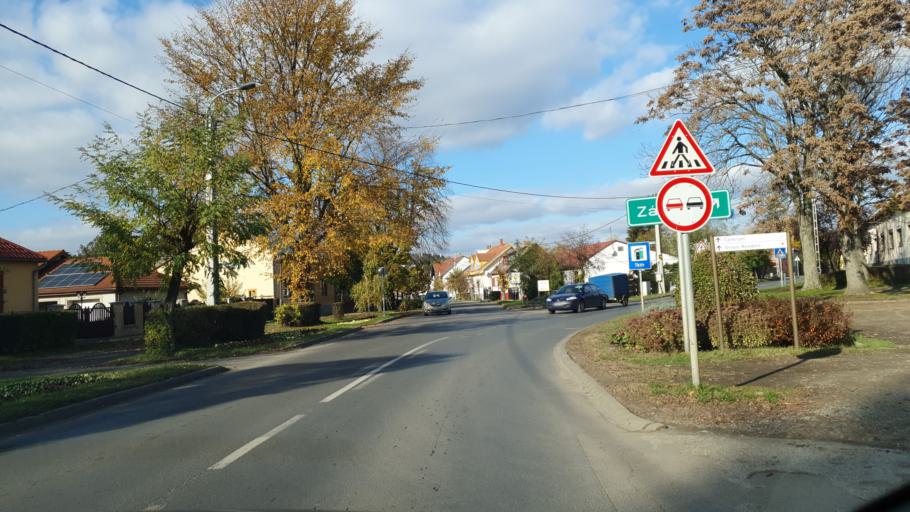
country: HU
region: Szabolcs-Szatmar-Bereg
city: Kisvarda
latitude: 48.2179
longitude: 22.0824
